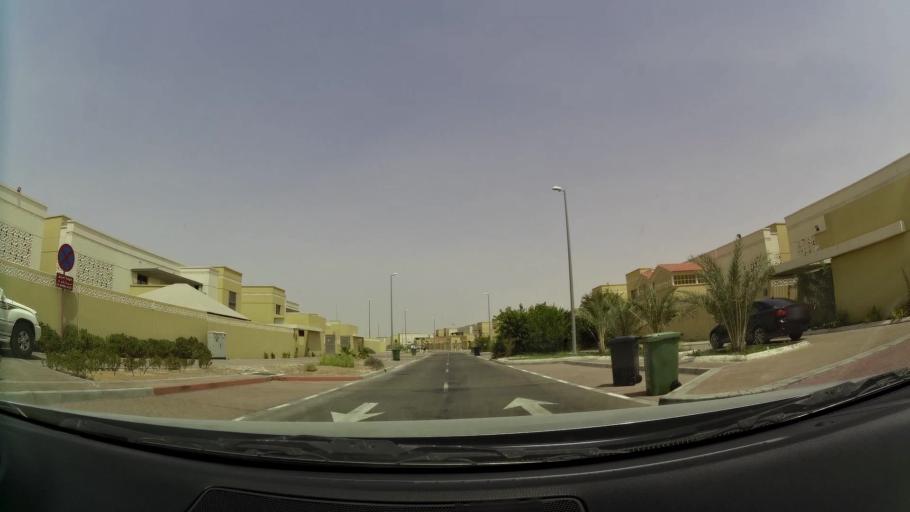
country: AE
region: Abu Dhabi
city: Al Ain
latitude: 24.1436
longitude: 55.6198
